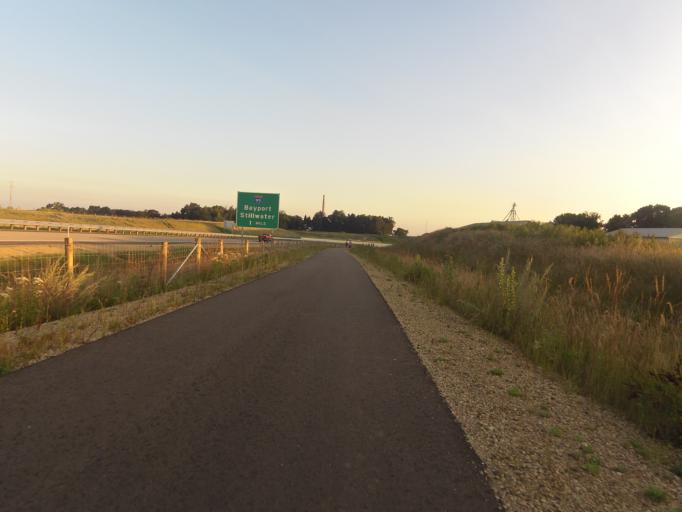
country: US
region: Minnesota
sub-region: Washington County
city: Oak Park Heights
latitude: 45.0508
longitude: -92.7792
